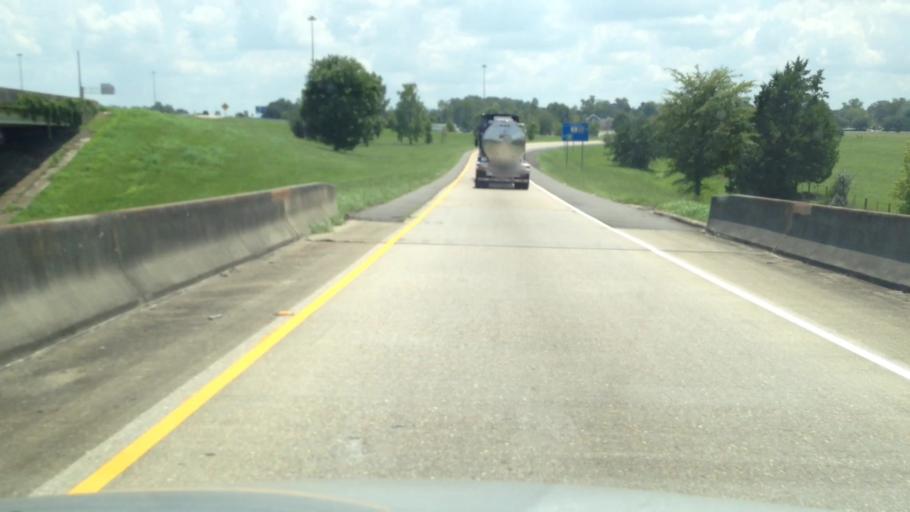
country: US
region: Louisiana
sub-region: Saint Landry Parish
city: Opelousas
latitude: 30.5357
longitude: -92.0649
